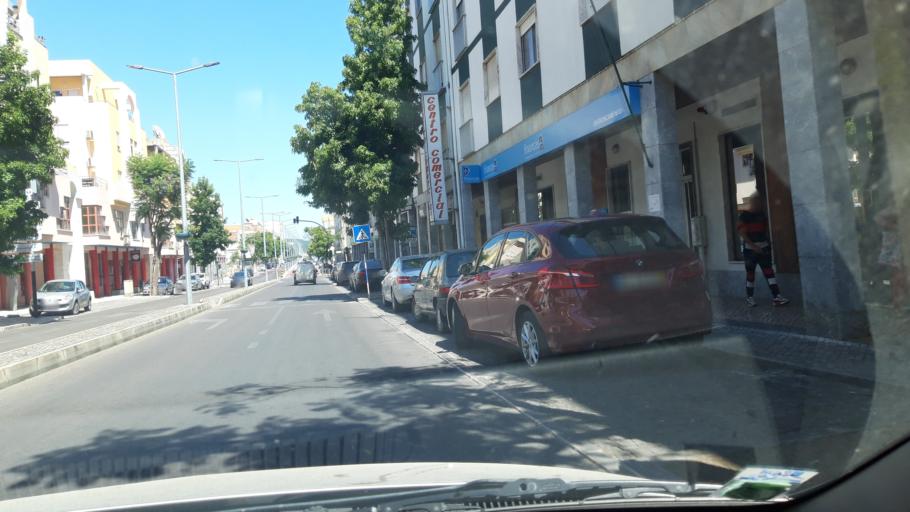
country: PT
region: Santarem
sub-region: Entroncamento
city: Entroncamento
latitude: 39.4611
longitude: -8.4710
